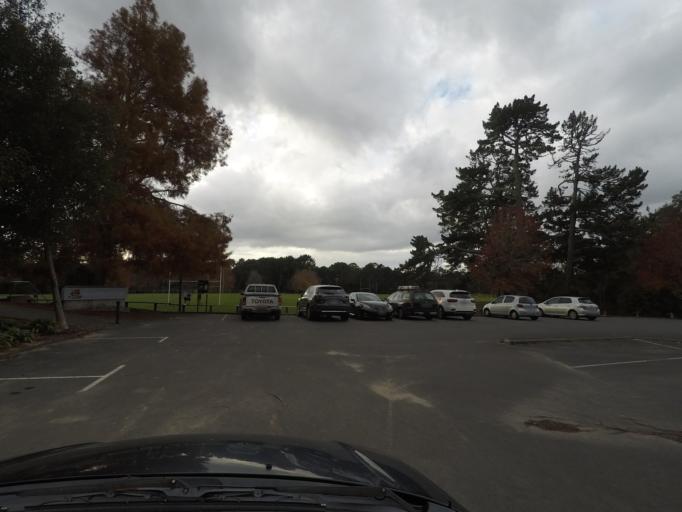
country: NZ
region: Auckland
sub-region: Auckland
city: Rosebank
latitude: -36.8286
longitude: 174.6296
